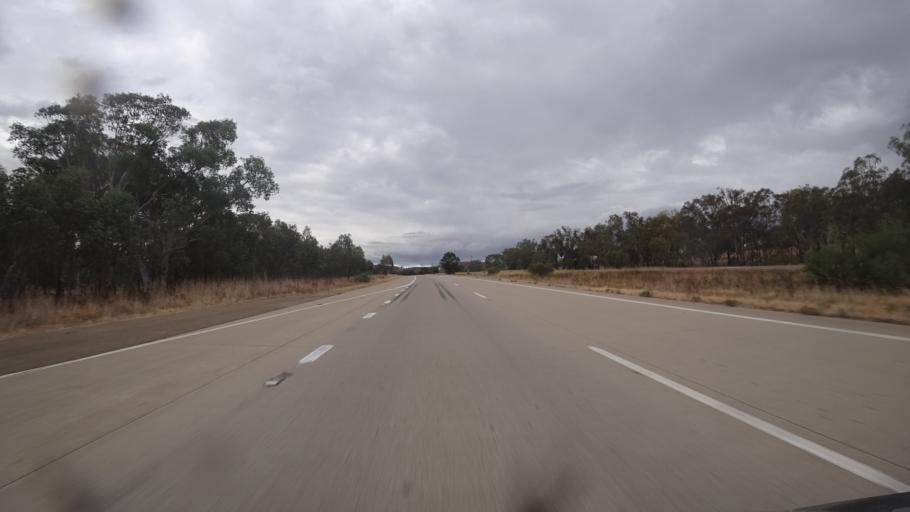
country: AU
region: New South Wales
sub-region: Yass Valley
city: Yass
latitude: -34.8097
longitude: 148.6890
